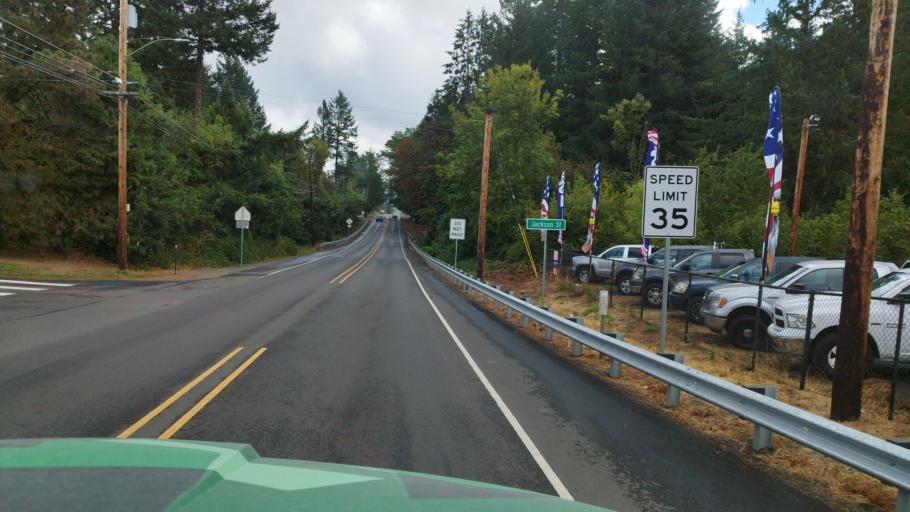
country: US
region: Oregon
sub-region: Yamhill County
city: Lafayette
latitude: 45.2431
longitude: -123.1101
